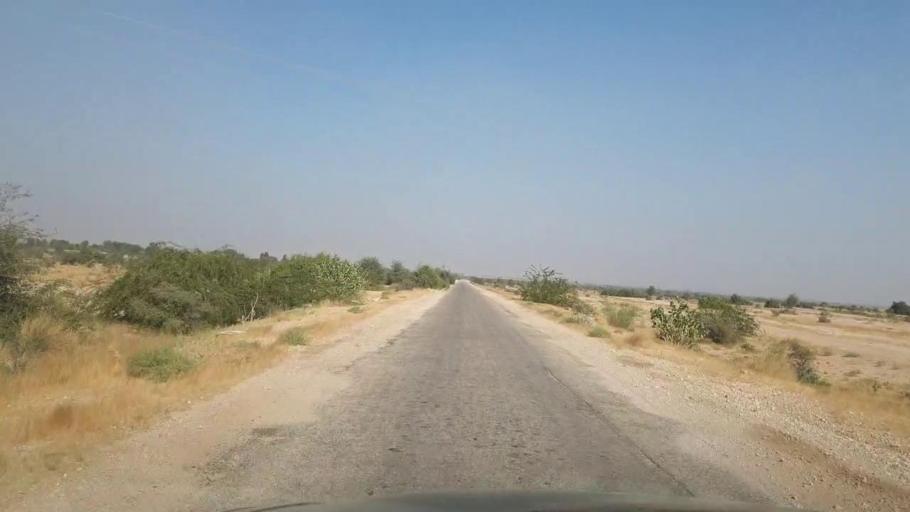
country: PK
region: Sindh
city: Jamshoro
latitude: 25.4692
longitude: 67.8145
